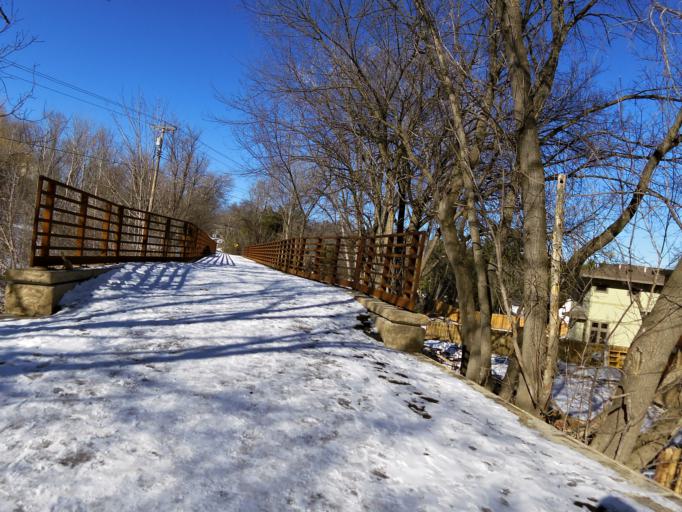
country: US
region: Minnesota
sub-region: Washington County
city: Stillwater
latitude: 45.0728
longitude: -92.8072
